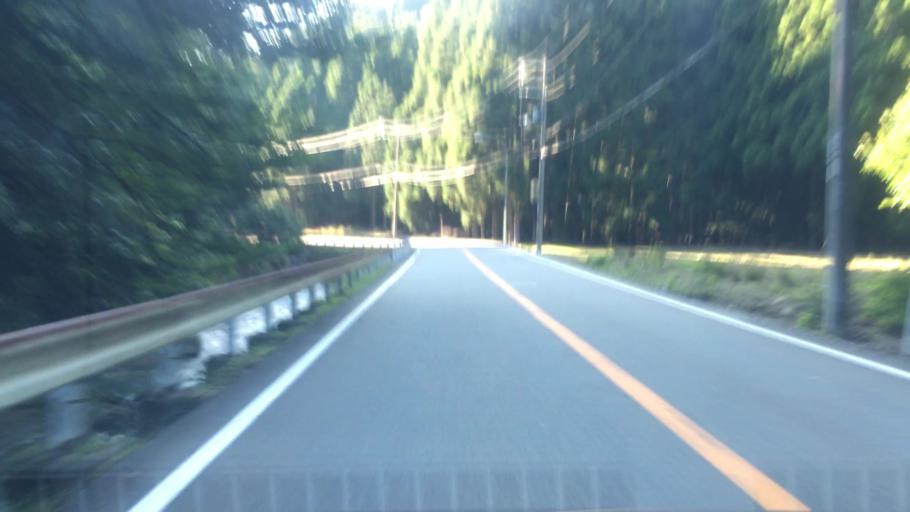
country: JP
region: Hyogo
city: Toyooka
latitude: 35.6166
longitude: 134.8569
